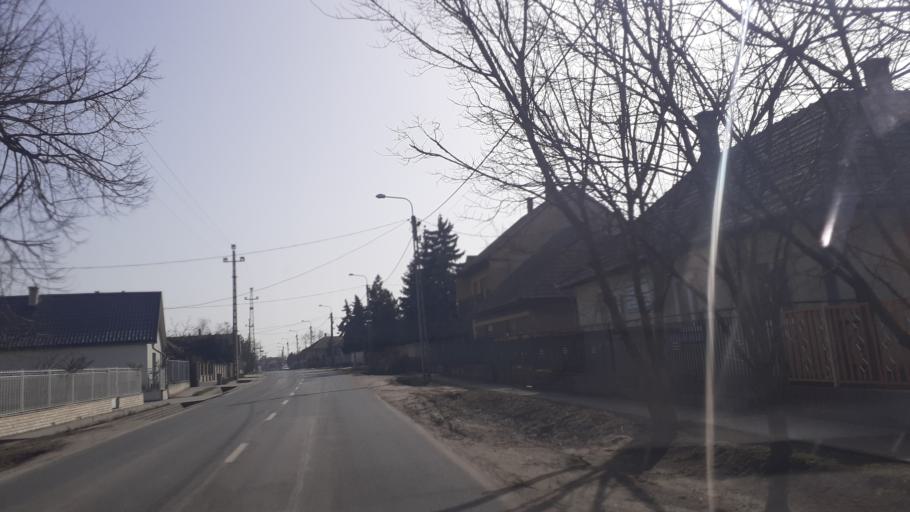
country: HU
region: Pest
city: Bugyi
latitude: 47.2240
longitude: 19.1434
